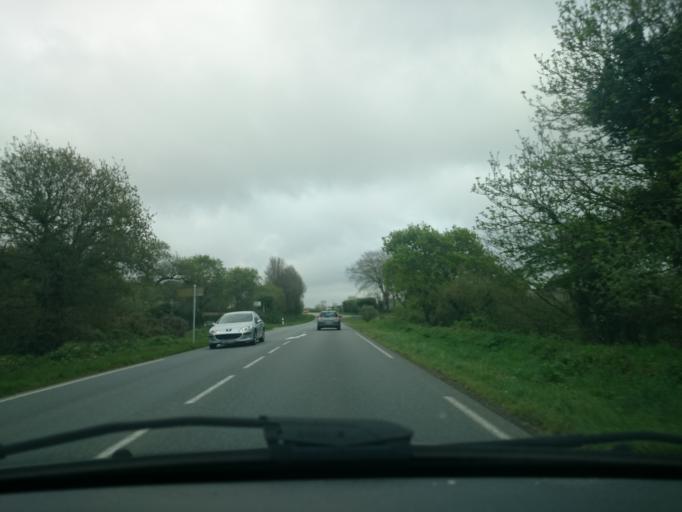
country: FR
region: Brittany
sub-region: Departement du Finistere
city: Saint-Renan
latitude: 48.4323
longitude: -4.6116
